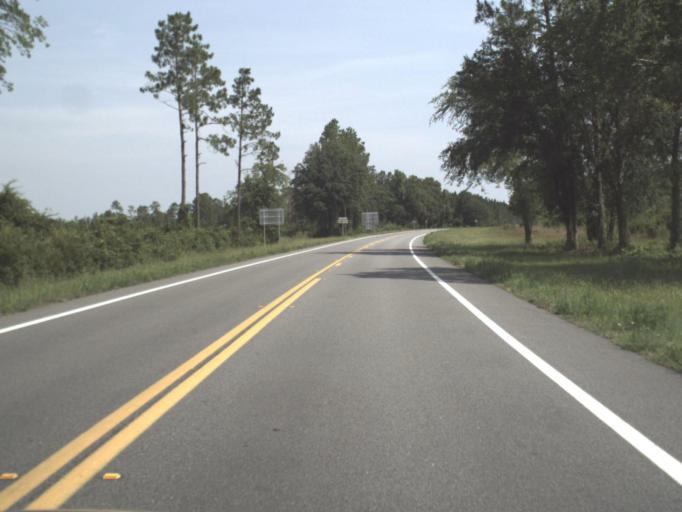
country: US
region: Georgia
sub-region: Echols County
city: Statenville
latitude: 30.6133
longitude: -83.0228
